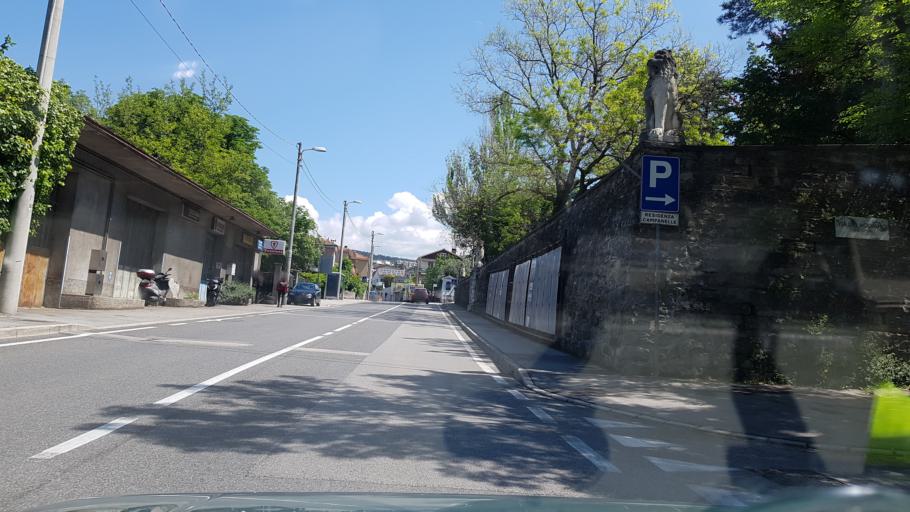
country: IT
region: Friuli Venezia Giulia
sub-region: Provincia di Trieste
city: Trieste
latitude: 45.6372
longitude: 13.8006
